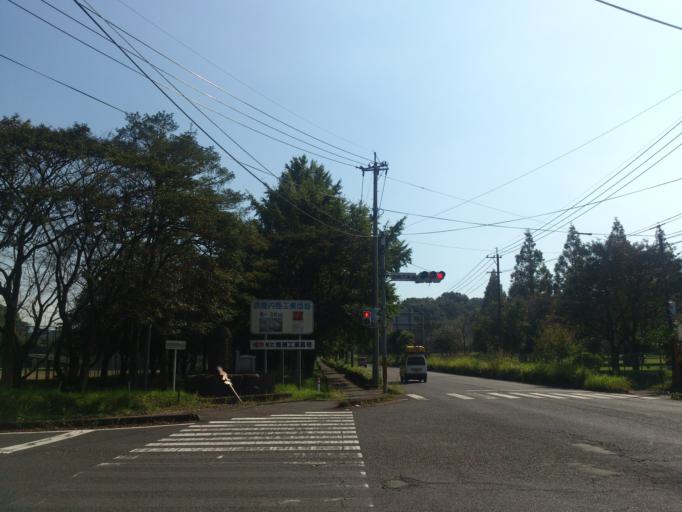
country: JP
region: Kagoshima
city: Kanoya
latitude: 31.3700
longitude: 130.8578
